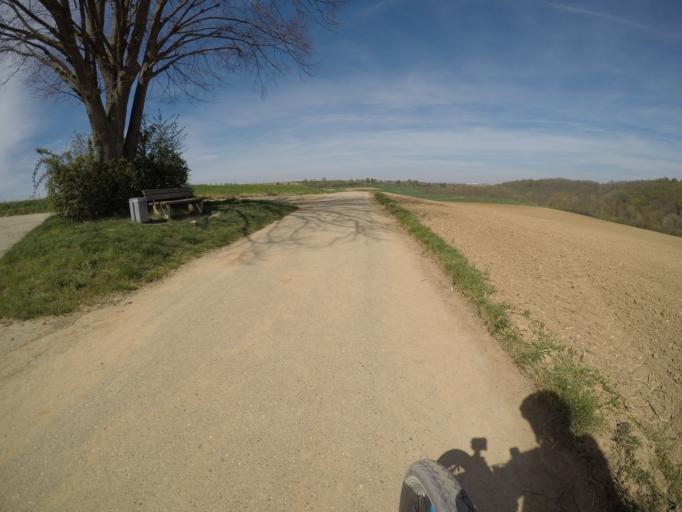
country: DE
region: Baden-Wuerttemberg
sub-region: Regierungsbezirk Stuttgart
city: Hemmingen
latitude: 48.8499
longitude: 9.0440
